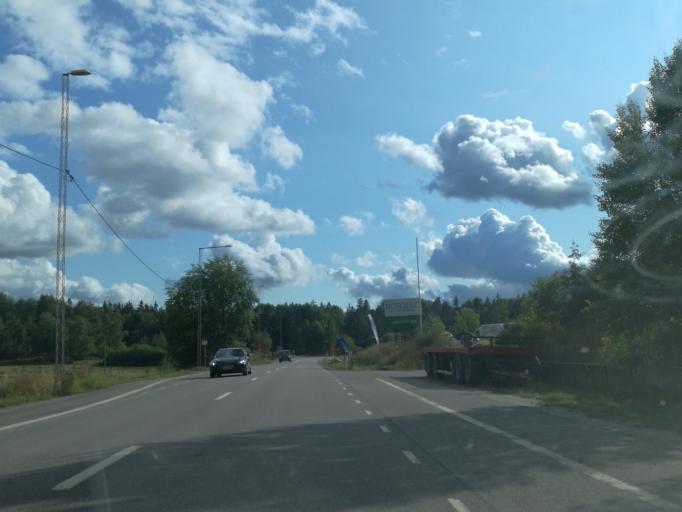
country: SE
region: Stockholm
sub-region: Upplands Vasby Kommun
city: Upplands Vaesby
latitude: 59.5320
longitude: 17.9901
